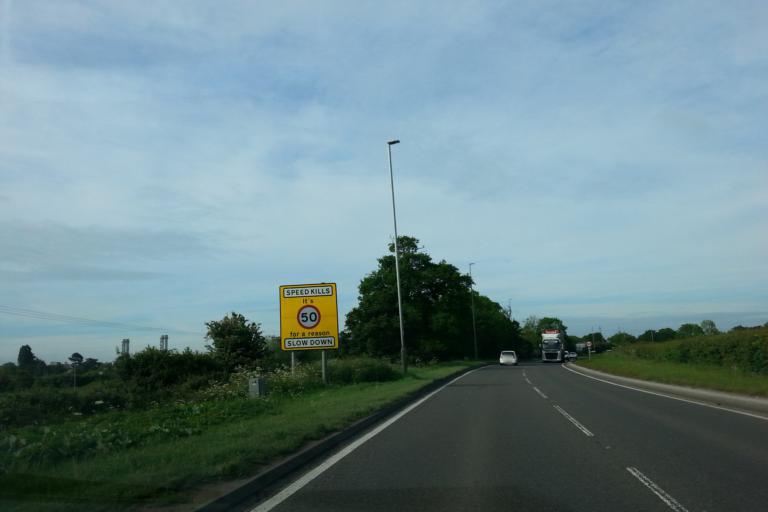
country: GB
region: England
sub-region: Nottinghamshire
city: Farndon
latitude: 53.0857
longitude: -0.8555
